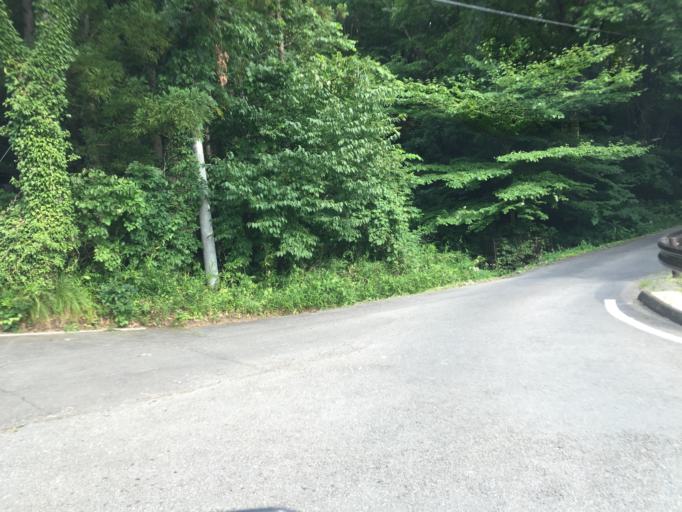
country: JP
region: Fukushima
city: Fukushima-shi
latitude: 37.7305
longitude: 140.4805
